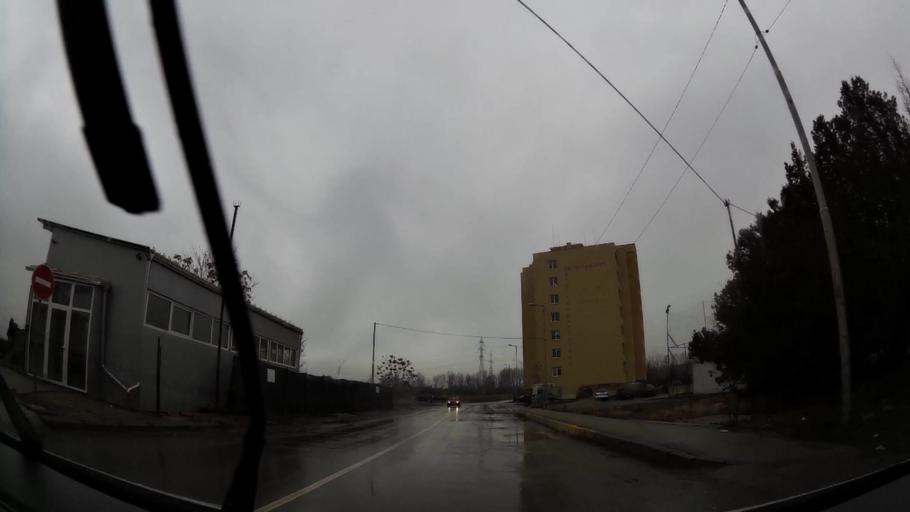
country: BG
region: Sofia-Capital
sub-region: Stolichna Obshtina
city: Sofia
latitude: 42.6254
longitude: 23.3850
